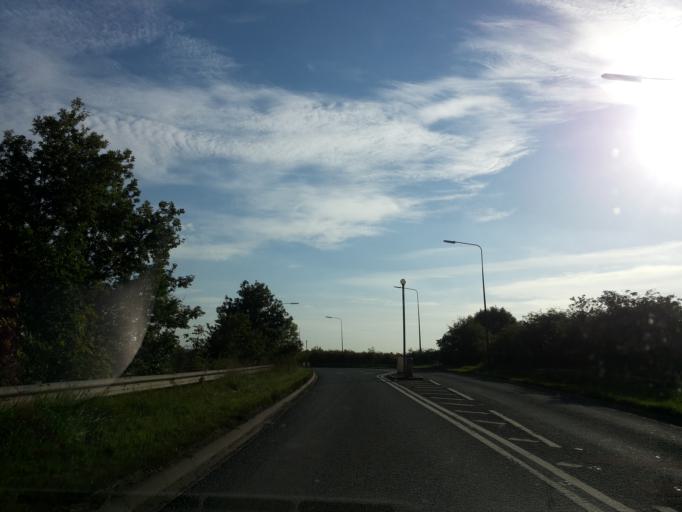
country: GB
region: England
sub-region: Doncaster
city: Hatfield
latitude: 53.5894
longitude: -0.9632
